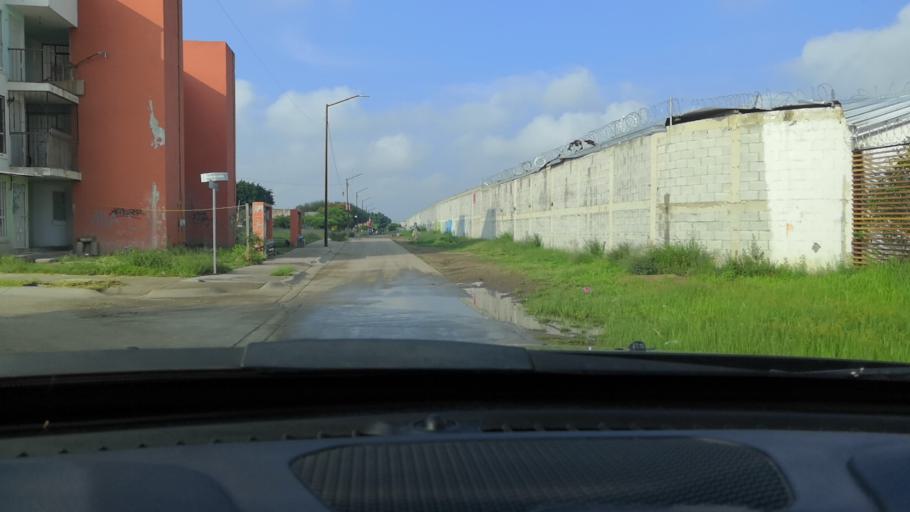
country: MX
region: Guanajuato
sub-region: Leon
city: Fraccionamiento Paraiso Real
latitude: 21.1039
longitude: -101.5868
